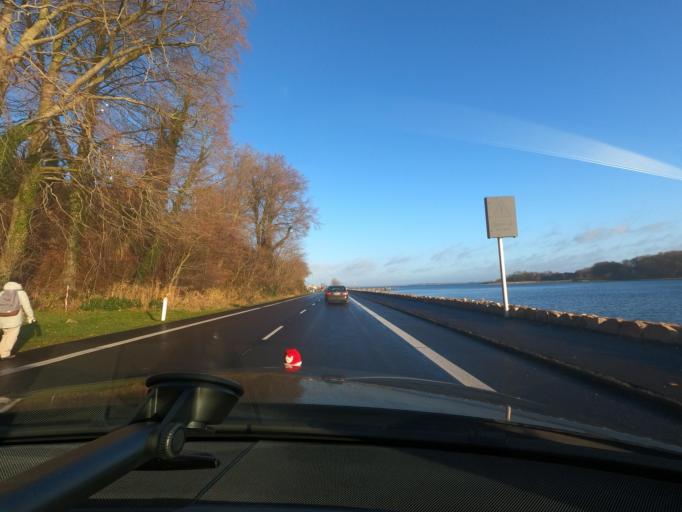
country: DE
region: Schleswig-Holstein
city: Wees
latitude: 54.8585
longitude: 9.4932
